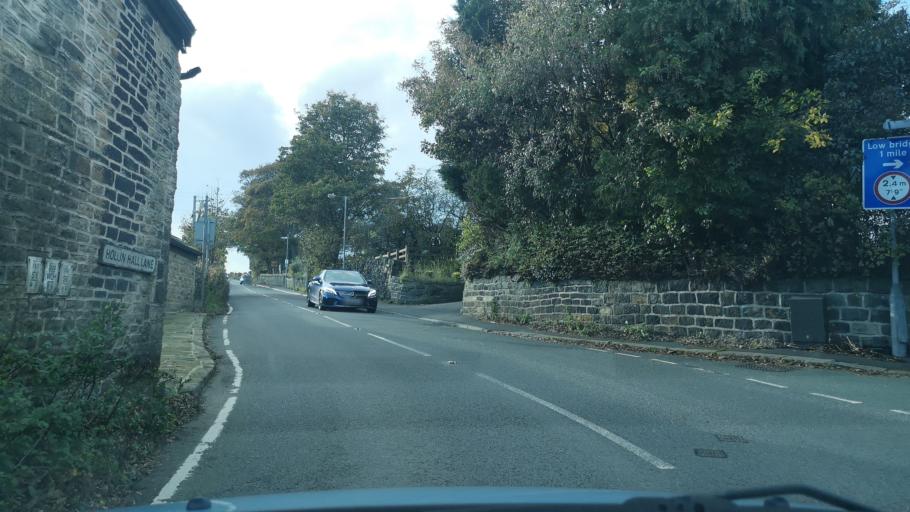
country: GB
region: England
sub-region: Kirklees
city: Mirfield
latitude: 53.6660
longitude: -1.7143
